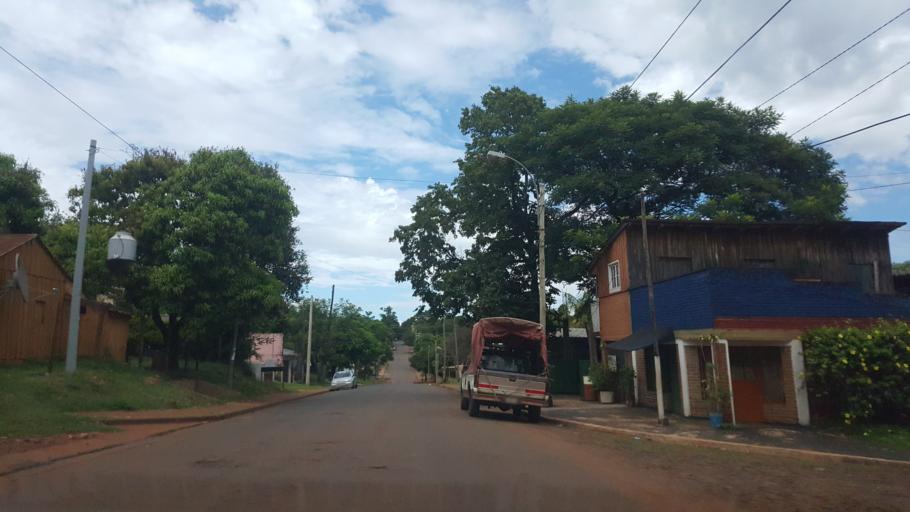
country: AR
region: Misiones
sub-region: Departamento de Capital
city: Posadas
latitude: -27.4266
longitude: -55.8870
